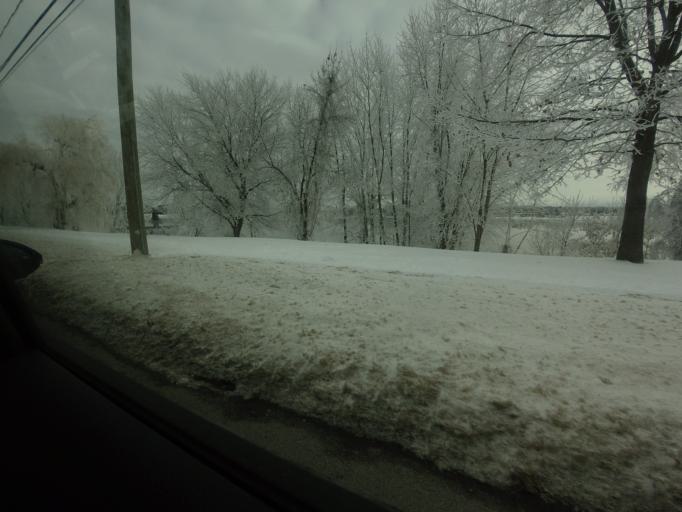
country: CA
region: New Brunswick
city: Fredericton
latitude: 45.9534
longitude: -66.6325
